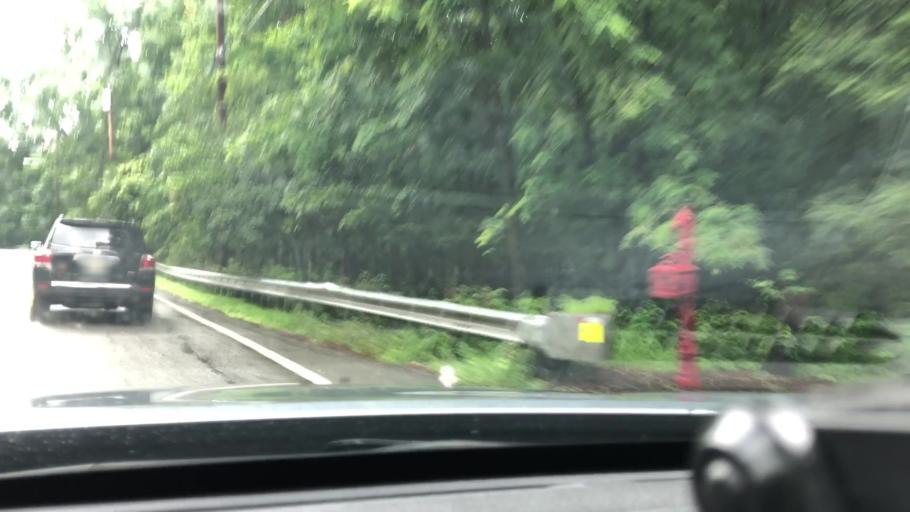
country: US
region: New Jersey
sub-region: Bergen County
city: Saddle River
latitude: 41.0260
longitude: -74.1022
